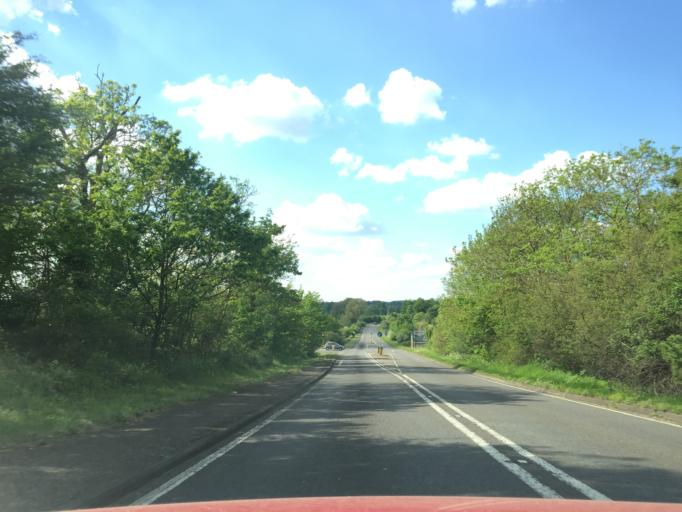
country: GB
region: England
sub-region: Northamptonshire
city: Roade
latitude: 52.1224
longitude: -0.9055
